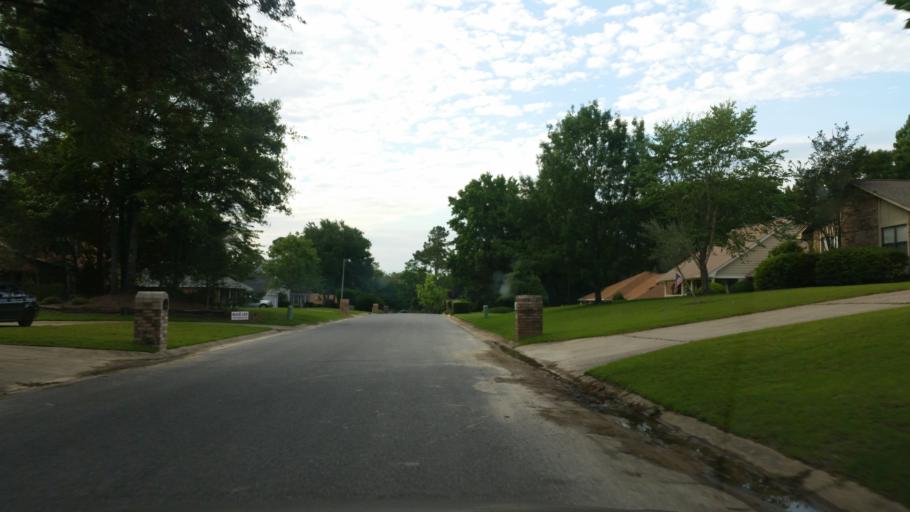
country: US
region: Florida
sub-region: Escambia County
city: Ferry Pass
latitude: 30.5087
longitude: -87.1711
